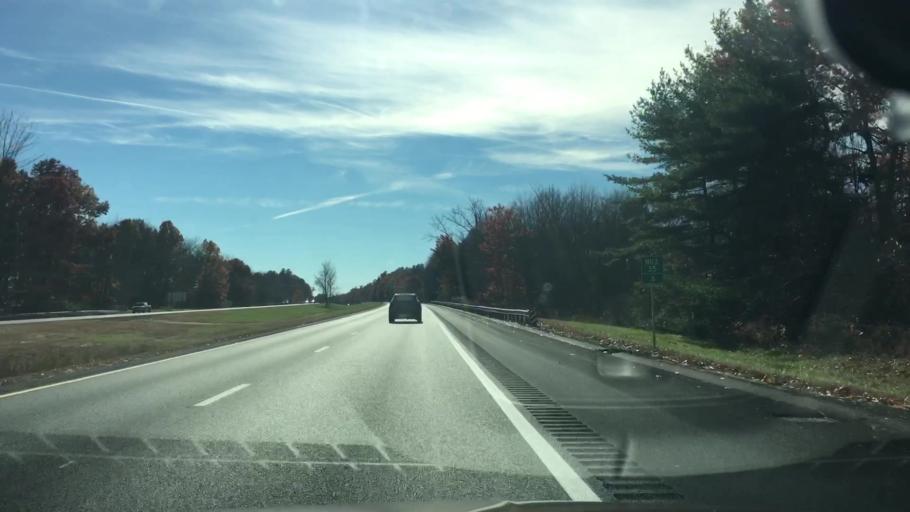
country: US
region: Massachusetts
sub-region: Franklin County
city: South Deerfield
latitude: 42.4800
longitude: -72.6171
